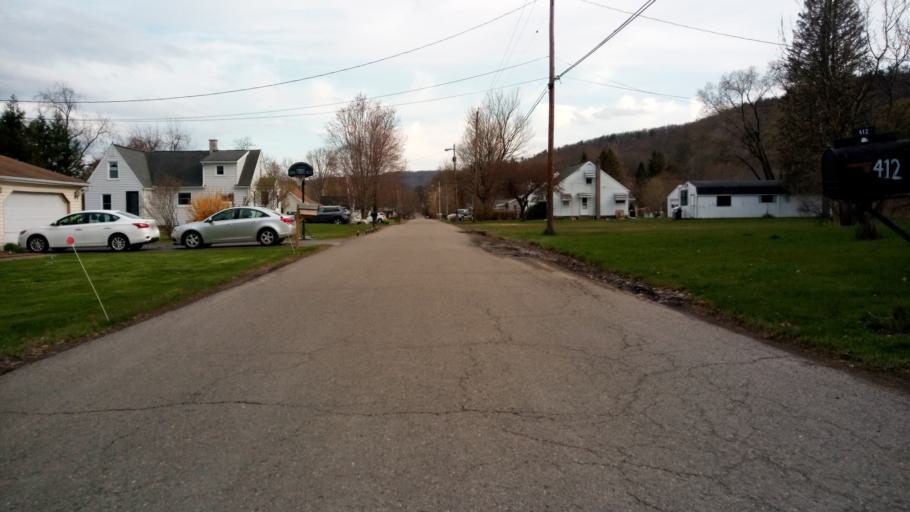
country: US
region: New York
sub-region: Chemung County
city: Southport
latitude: 42.0738
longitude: -76.8246
